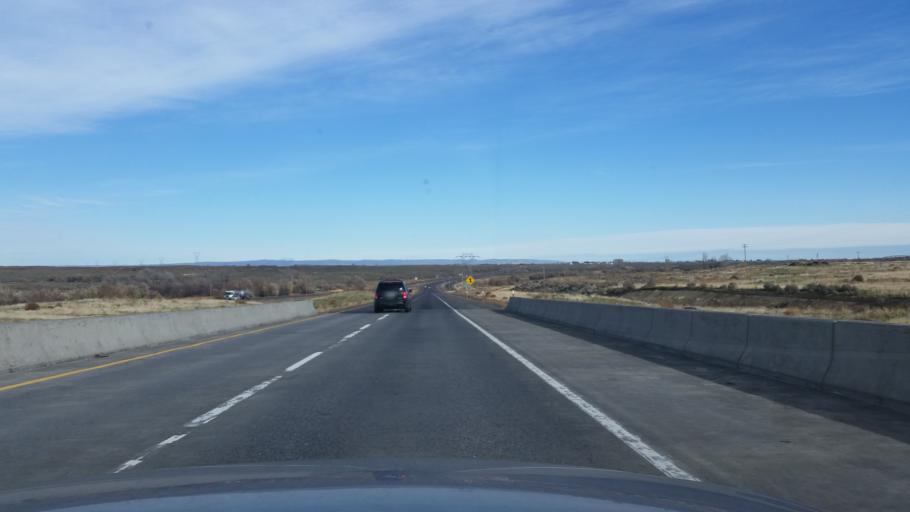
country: US
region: Washington
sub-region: Grant County
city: Quincy
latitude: 47.0205
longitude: -119.9443
